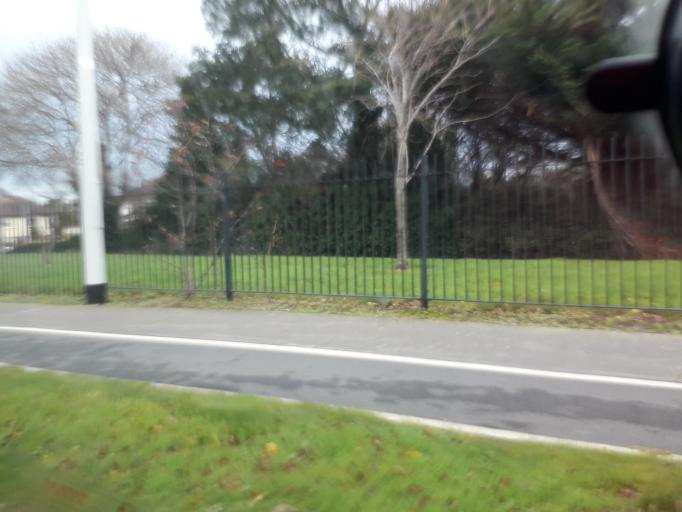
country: IE
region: Leinster
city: Sandyford
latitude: 53.2882
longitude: -6.2261
